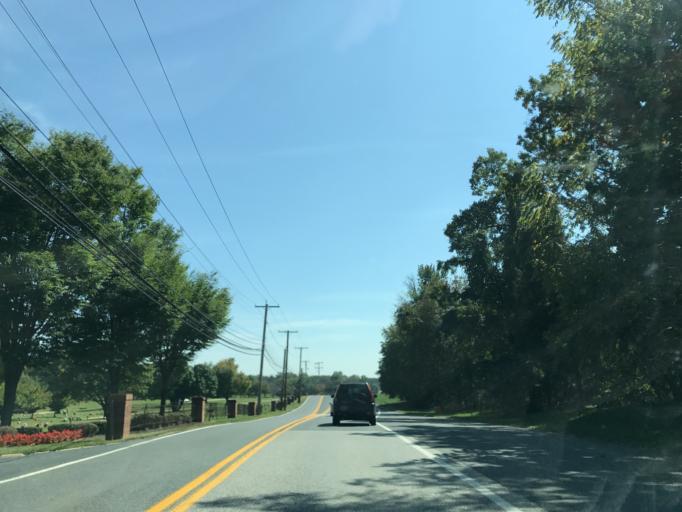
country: US
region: Maryland
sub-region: Anne Arundel County
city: Jessup
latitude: 39.1897
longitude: -76.7699
